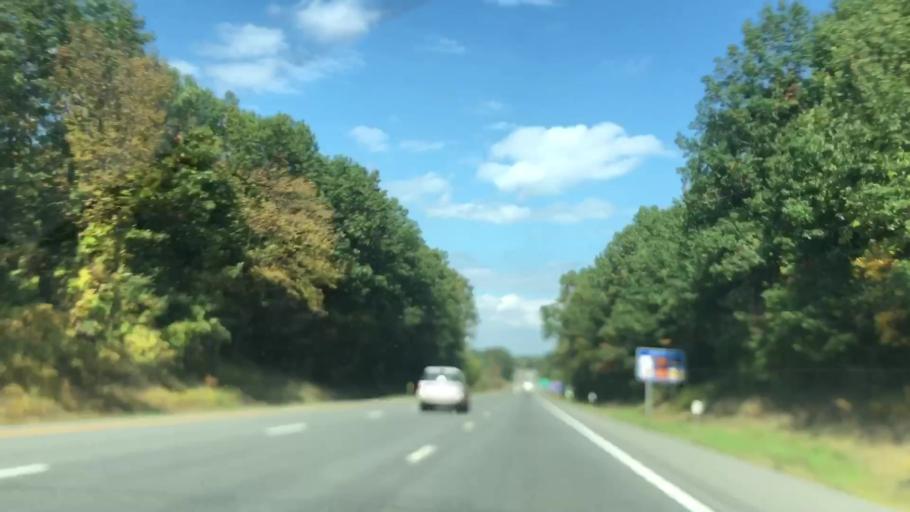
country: US
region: New York
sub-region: Saratoga County
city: Saratoga Springs
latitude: 43.0869
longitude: -73.7490
